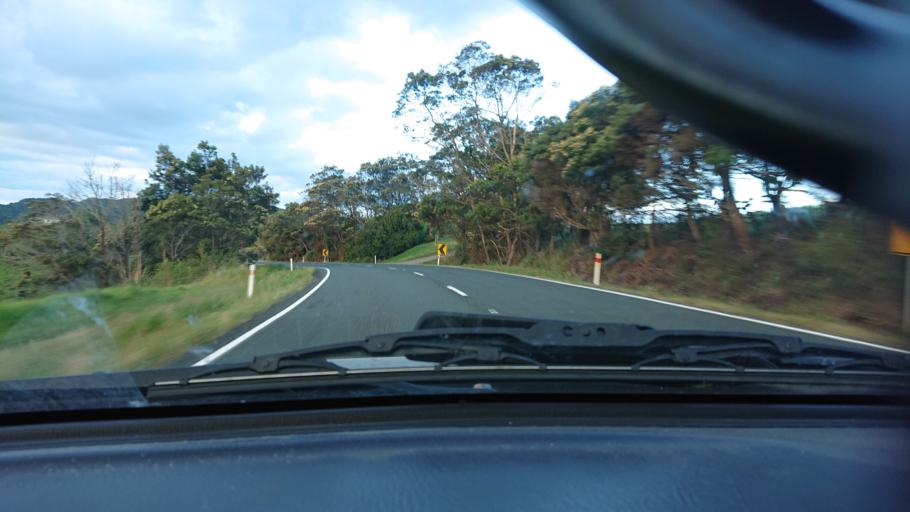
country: NZ
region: Auckland
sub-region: Auckland
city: Parakai
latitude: -36.4732
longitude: 174.4494
